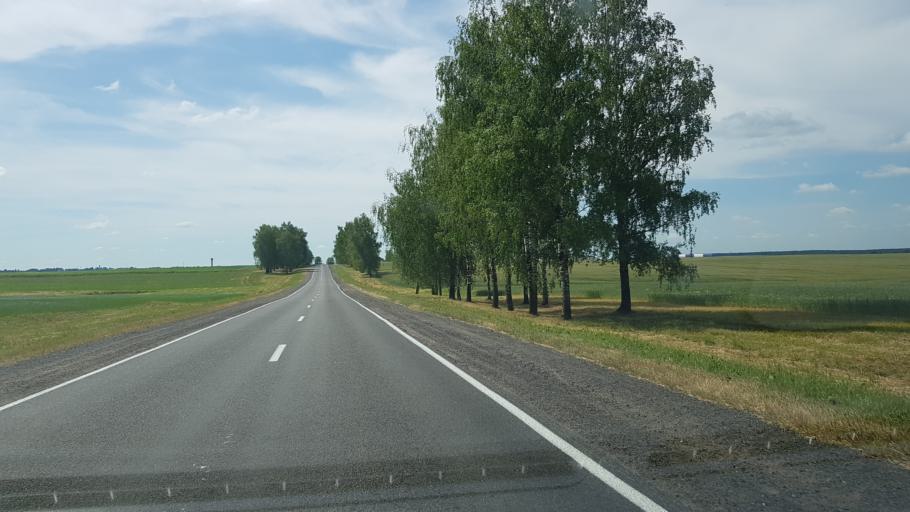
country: BY
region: Vitebsk
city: Dubrowna
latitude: 54.6034
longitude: 30.6730
